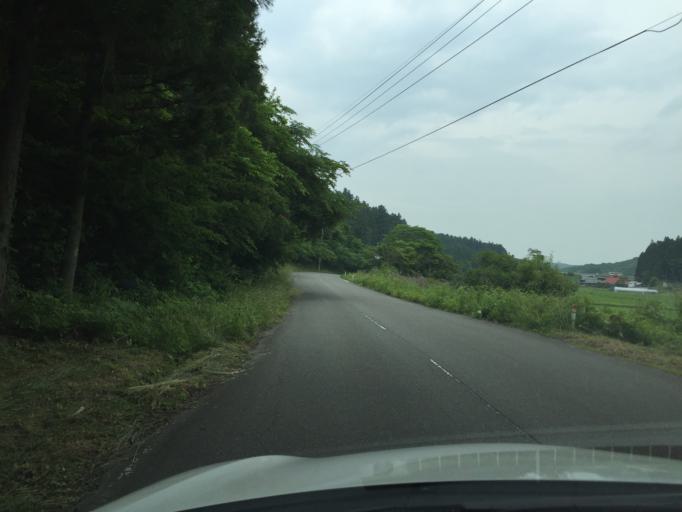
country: JP
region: Fukushima
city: Iwaki
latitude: 37.1743
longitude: 140.7135
